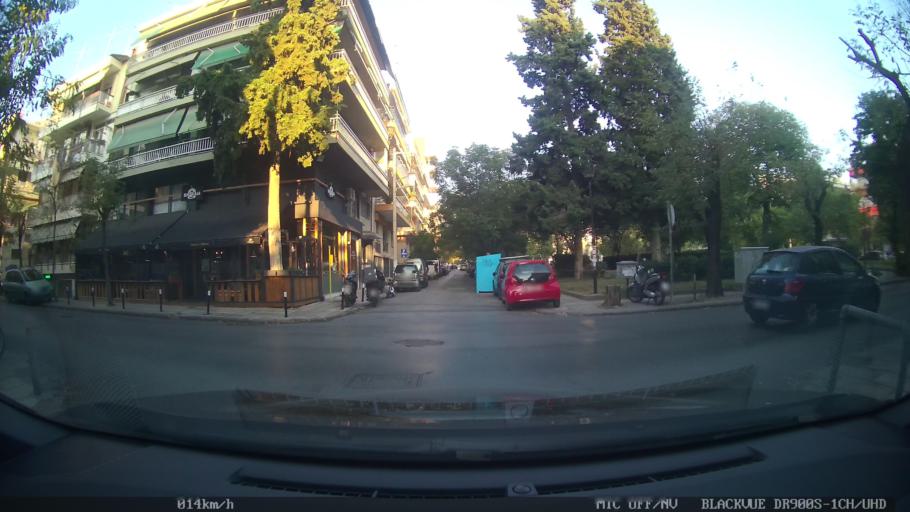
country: GR
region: Central Macedonia
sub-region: Nomos Thessalonikis
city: Triandria
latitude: 40.6026
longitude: 22.9720
